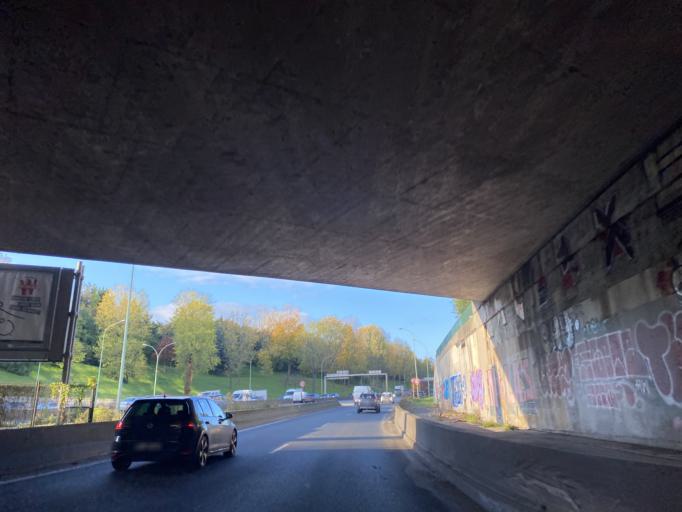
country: FR
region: Ile-de-France
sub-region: Departement de Seine-Saint-Denis
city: Bagnolet
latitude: 48.8674
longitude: 2.4138
